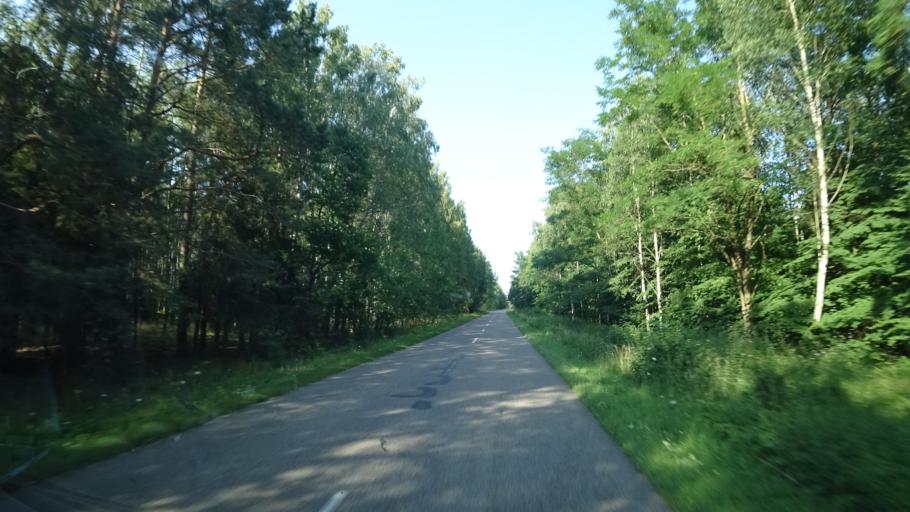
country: PL
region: Pomeranian Voivodeship
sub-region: Powiat czluchowski
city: Rzeczenica
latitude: 53.7719
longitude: 17.1506
